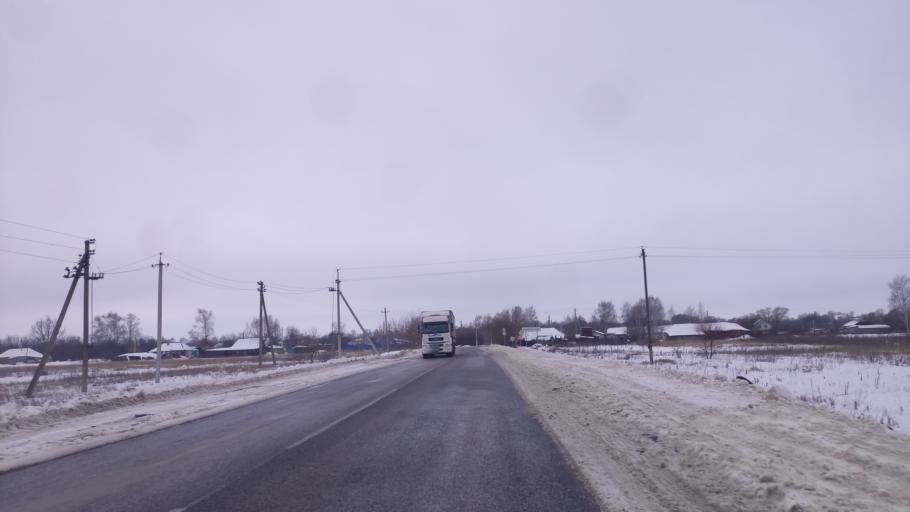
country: RU
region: Tambov
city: Pervomayskiy
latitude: 53.3045
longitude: 40.3841
